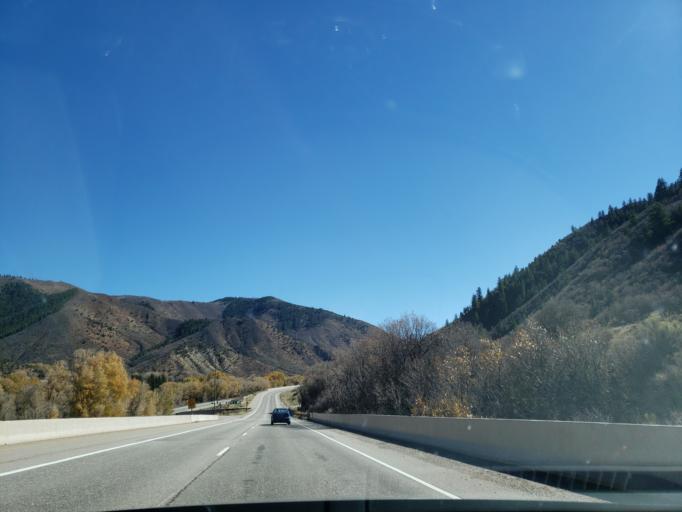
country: US
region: Colorado
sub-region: Eagle County
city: Basalt
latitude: 39.3250
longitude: -106.9517
